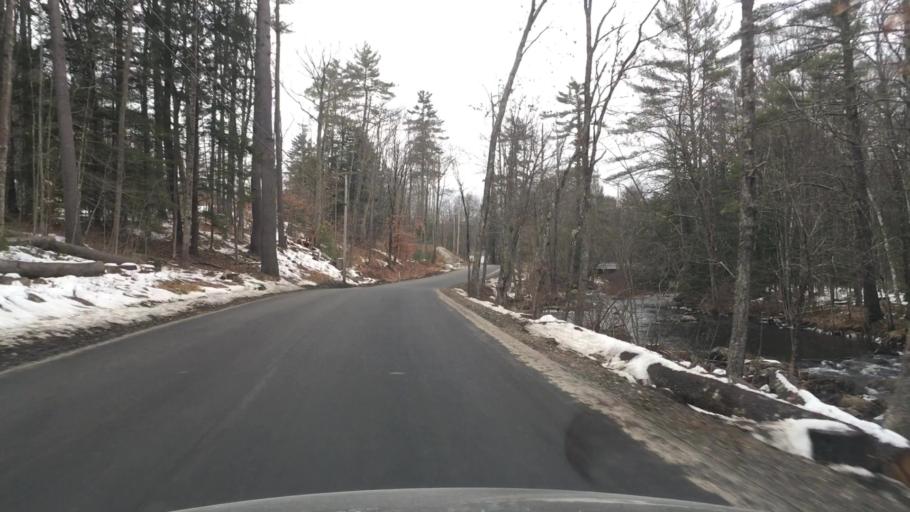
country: US
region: New Hampshire
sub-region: Hillsborough County
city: New Boston
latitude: 43.0039
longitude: -71.6638
